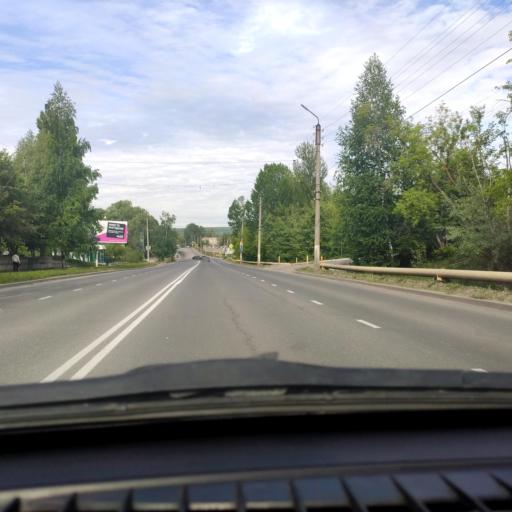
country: RU
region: Samara
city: Zhigulevsk
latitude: 53.4032
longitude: 49.5134
